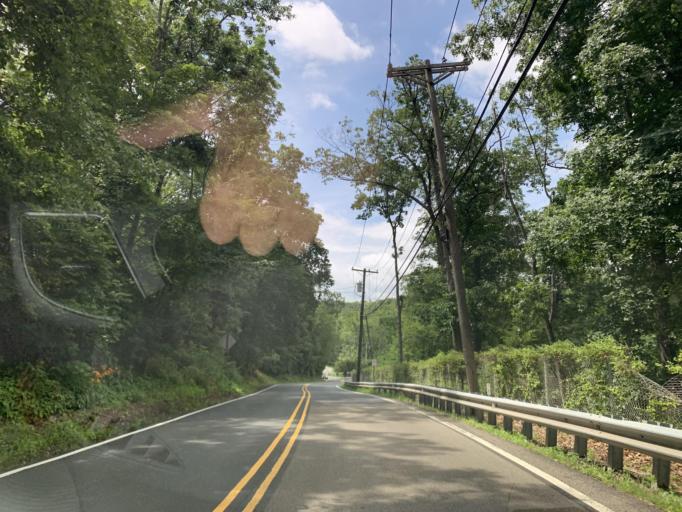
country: US
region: New Jersey
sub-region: Somerset County
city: Martinsville
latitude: 40.5915
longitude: -74.5632
